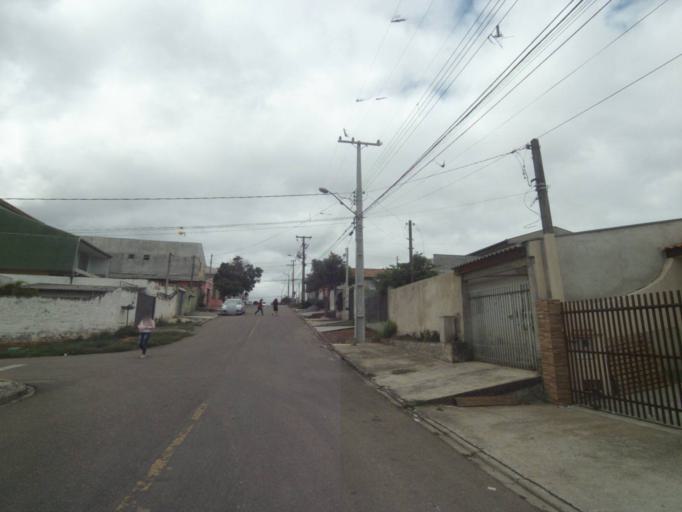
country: BR
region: Parana
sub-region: Sao Jose Dos Pinhais
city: Sao Jose dos Pinhais
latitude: -25.5459
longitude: -49.2712
